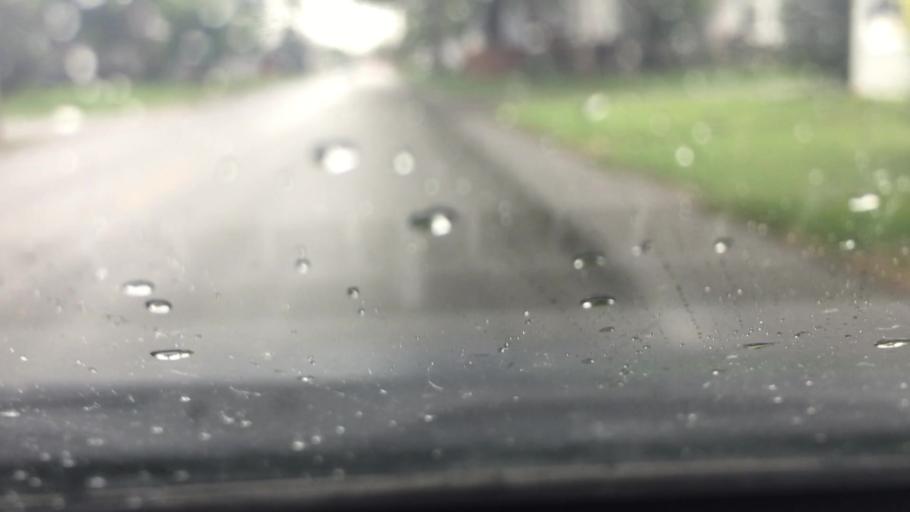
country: US
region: Illinois
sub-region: Williamson County
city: Marion
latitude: 37.7278
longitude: -88.9465
